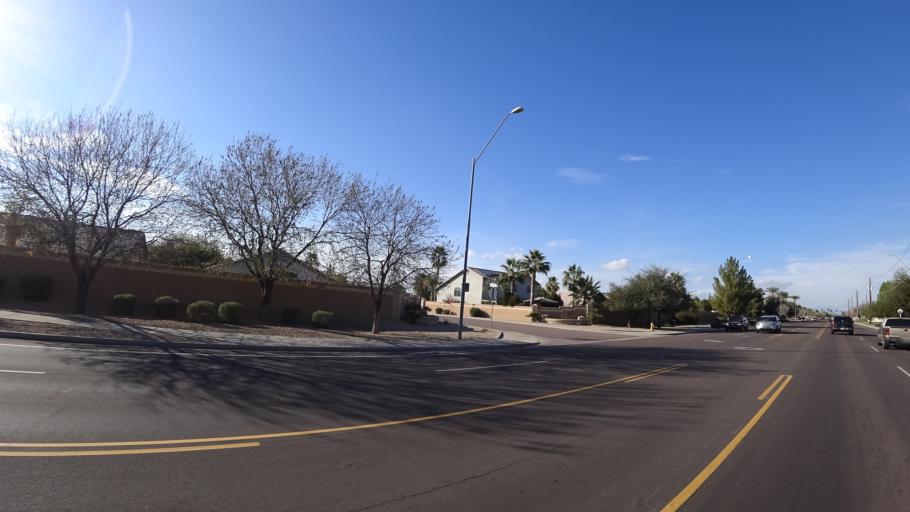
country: US
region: Arizona
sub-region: Maricopa County
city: Peoria
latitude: 33.5925
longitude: -112.2377
